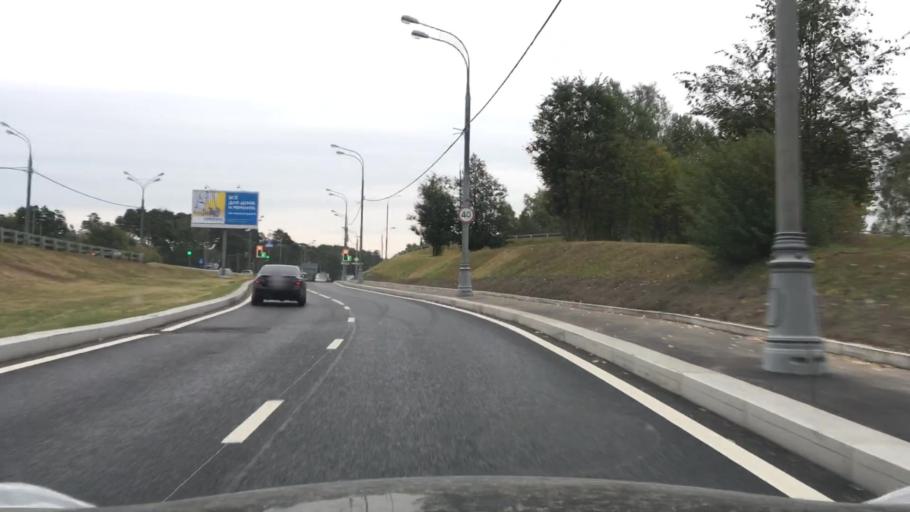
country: RU
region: Moscow
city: Rublevo
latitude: 55.7649
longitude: 37.3794
